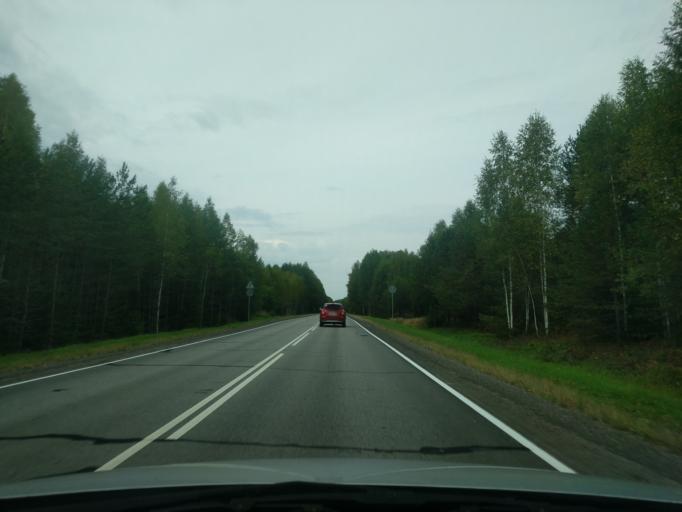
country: RU
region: Kirov
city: Kotel'nich
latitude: 58.2710
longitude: 48.0947
